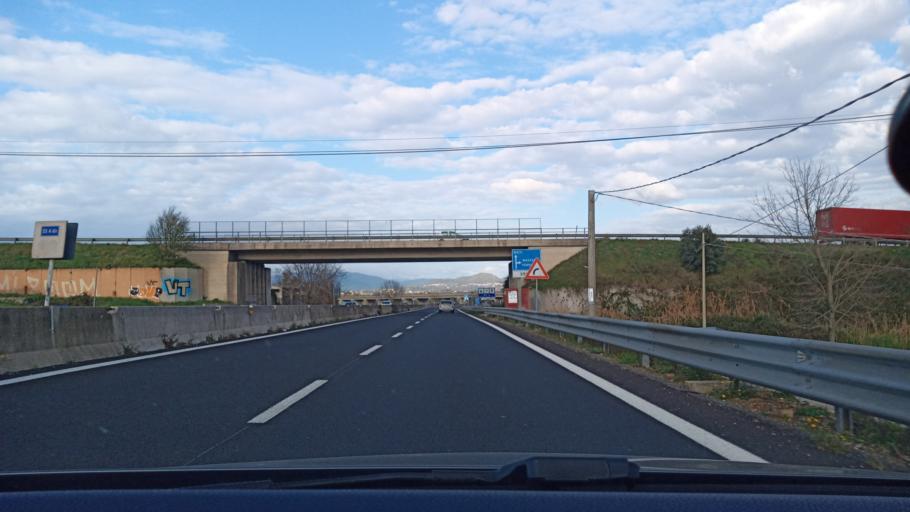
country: IT
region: Latium
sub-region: Citta metropolitana di Roma Capitale
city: Fiano Romano
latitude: 42.1470
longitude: 12.6190
